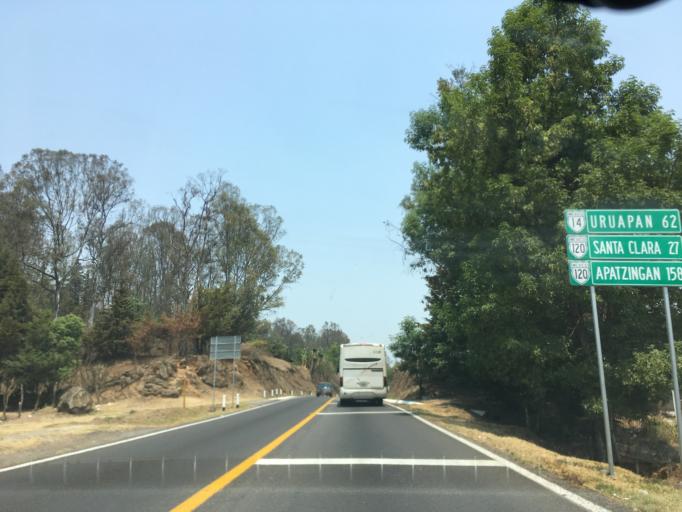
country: MX
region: Michoacan
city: Patzcuaro
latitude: 19.5452
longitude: -101.5896
